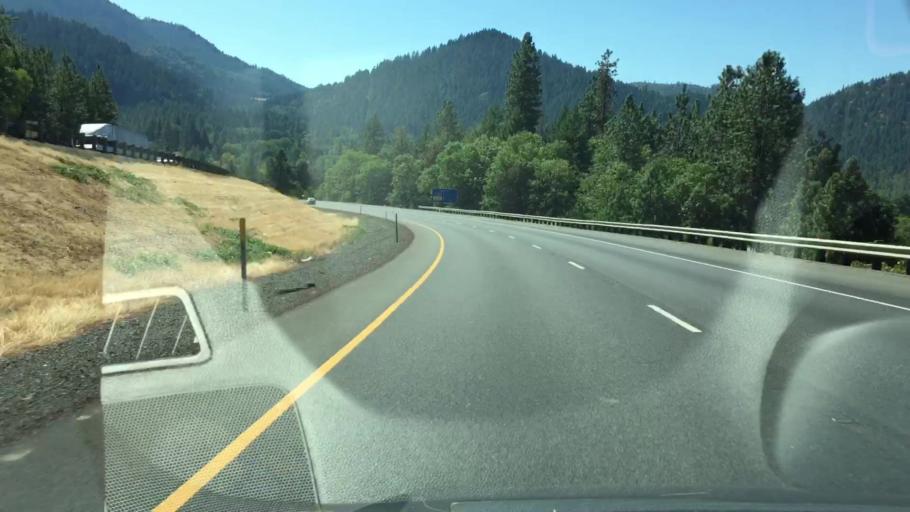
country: US
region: Oregon
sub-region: Josephine County
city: Merlin
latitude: 42.6420
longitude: -123.3880
